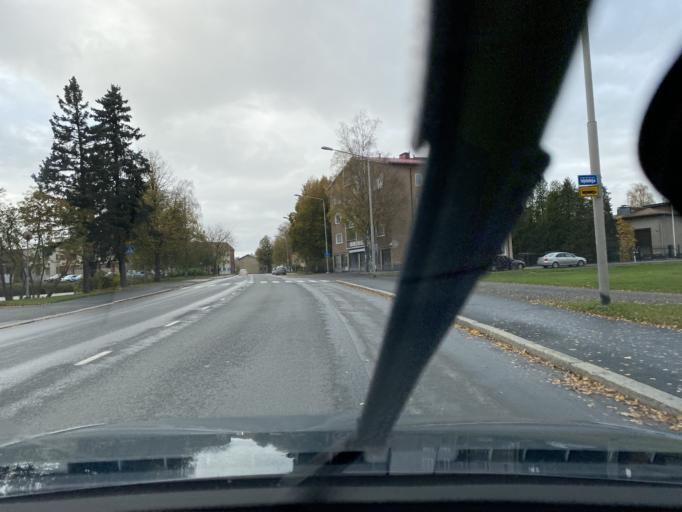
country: FI
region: Haeme
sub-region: Forssa
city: Forssa
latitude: 60.8153
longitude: 23.6171
